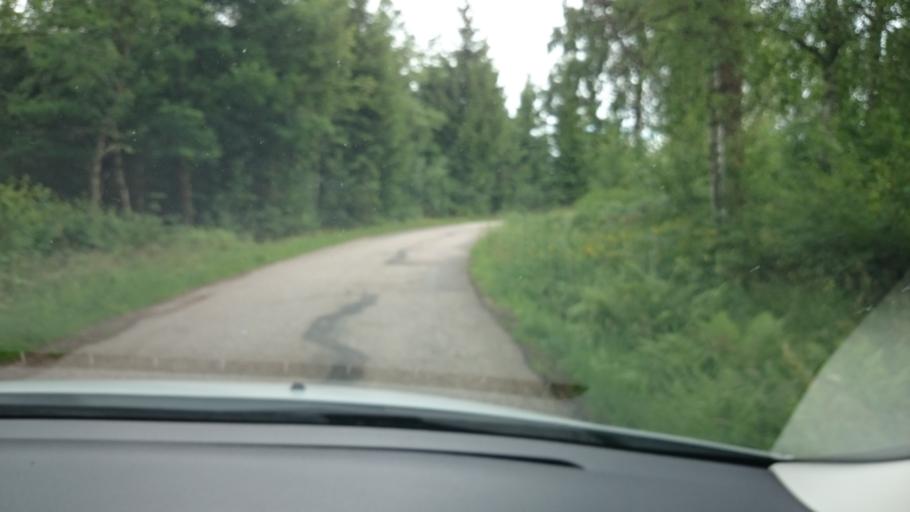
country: SE
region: Halland
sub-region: Hylte Kommun
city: Hyltebruk
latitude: 56.9699
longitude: 13.1970
